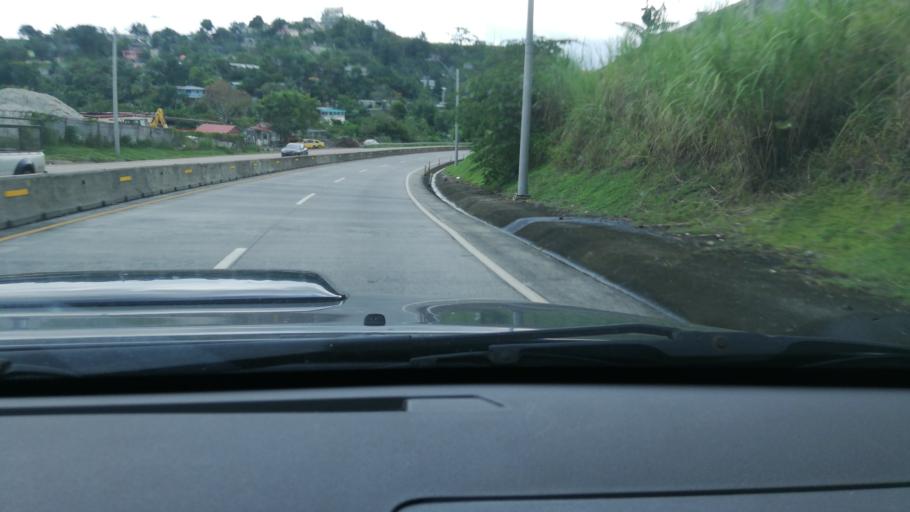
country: PA
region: Panama
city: San Miguelito
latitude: 9.0586
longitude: -79.4810
